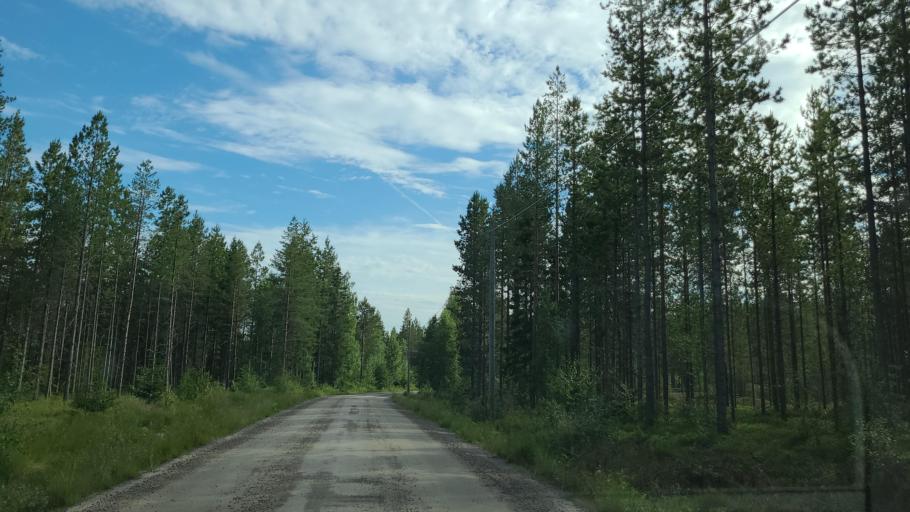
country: SE
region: Vaesterbotten
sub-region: Robertsfors Kommun
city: Robertsfors
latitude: 64.1590
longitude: 20.9421
